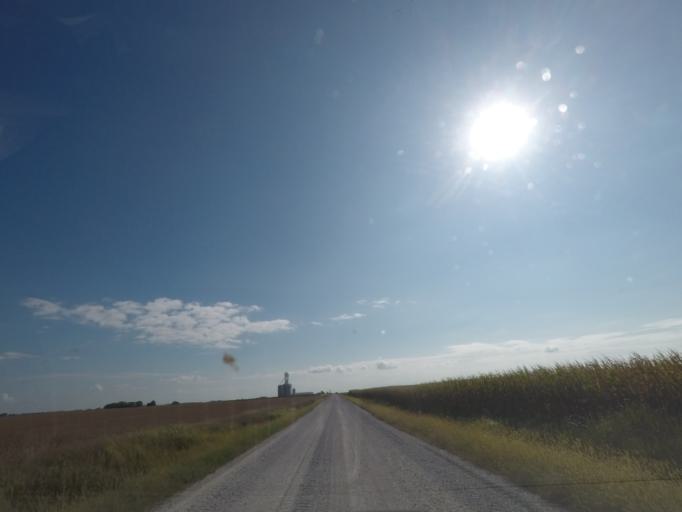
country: US
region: Iowa
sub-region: Story County
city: Nevada
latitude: 42.0490
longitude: -93.4187
